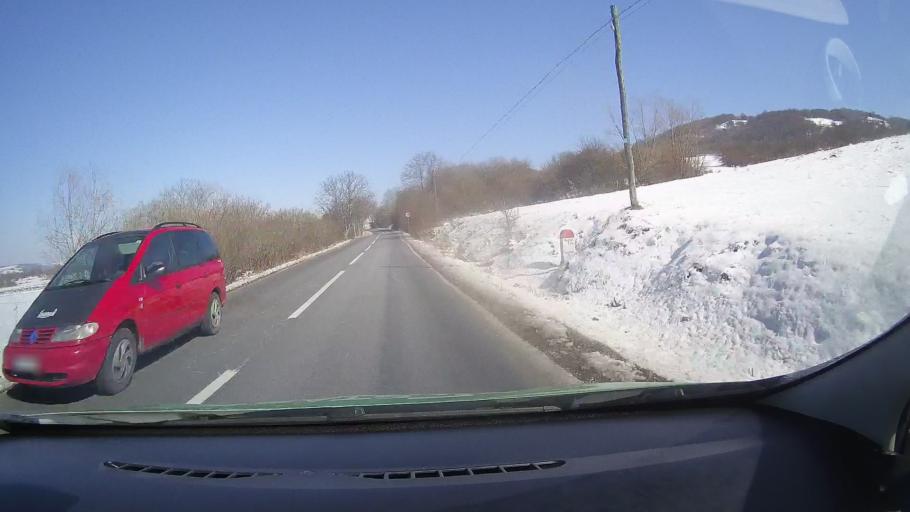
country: RO
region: Brasov
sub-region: Comuna Comana
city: Comana de Jos
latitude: 45.9291
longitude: 25.2494
